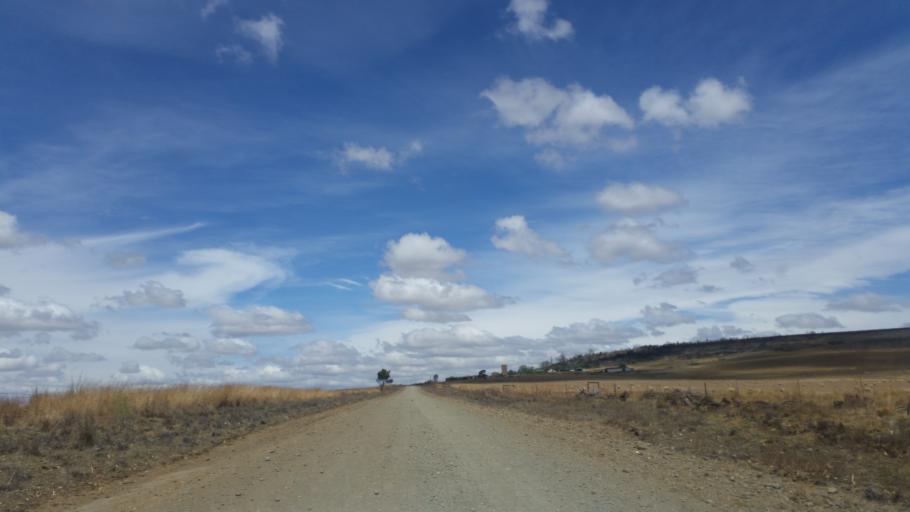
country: ZA
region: Orange Free State
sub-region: Thabo Mofutsanyana District Municipality
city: Bethlehem
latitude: -28.2449
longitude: 28.5808
